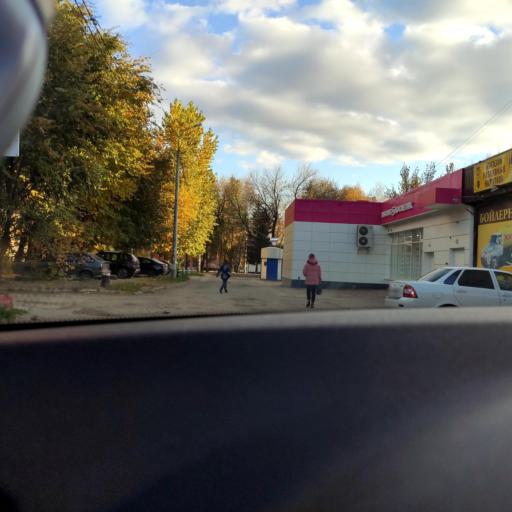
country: RU
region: Samara
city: Samara
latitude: 53.2321
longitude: 50.2591
